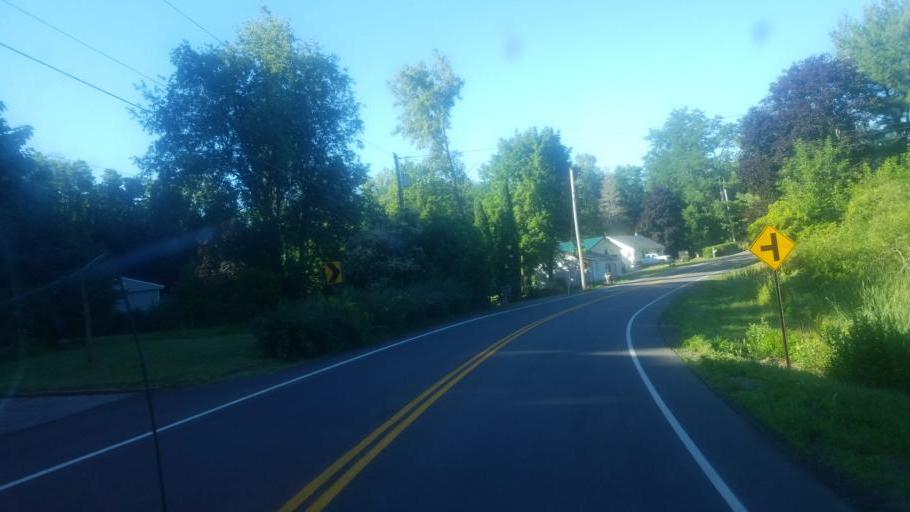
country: US
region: New York
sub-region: Wayne County
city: Newark
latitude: 43.0879
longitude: -77.0653
